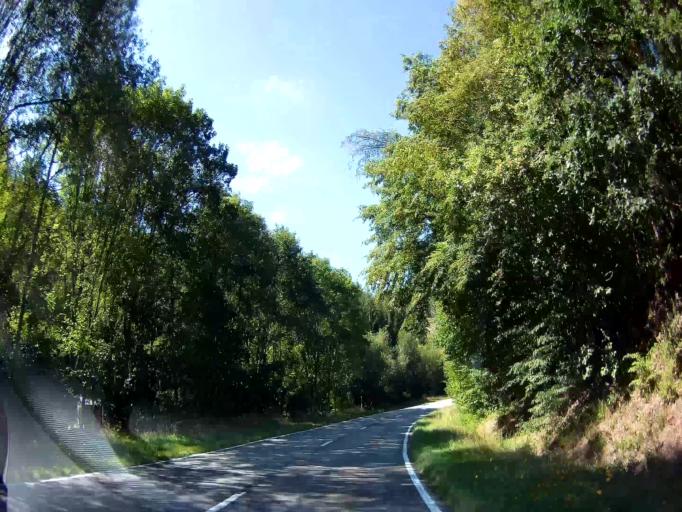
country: BE
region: Wallonia
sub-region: Province du Luxembourg
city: Bertogne
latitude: 50.1027
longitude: 5.6434
